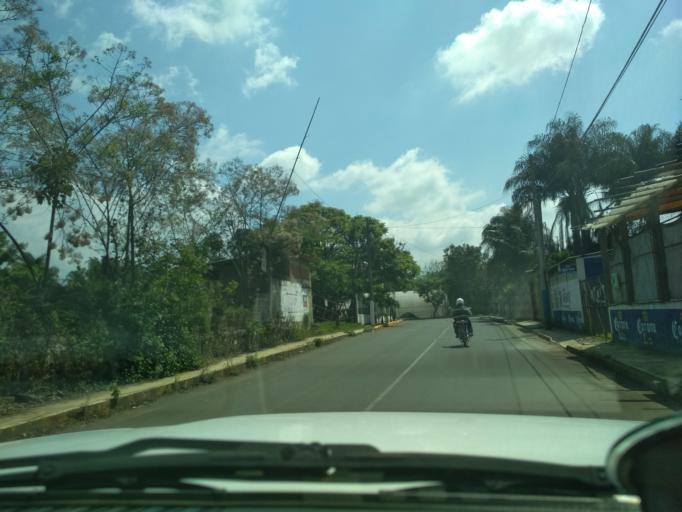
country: MX
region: Veracruz
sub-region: Fortin
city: Fraccionamiento los Alamos
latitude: 18.9169
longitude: -96.9765
